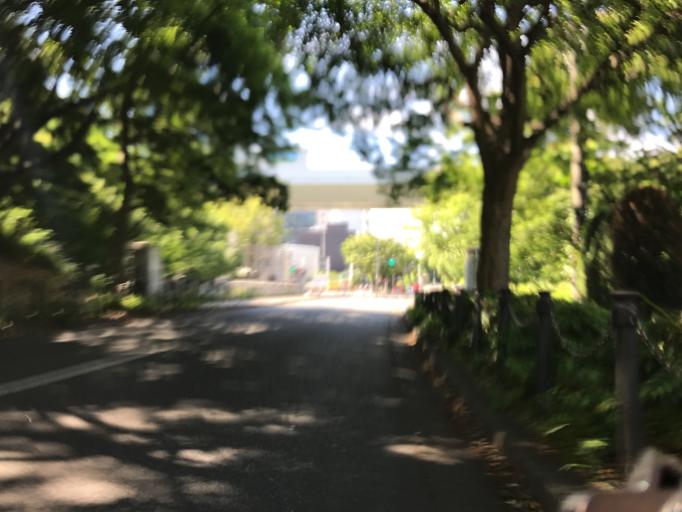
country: JP
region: Aichi
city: Nagoya-shi
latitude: 35.1789
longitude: 136.9081
